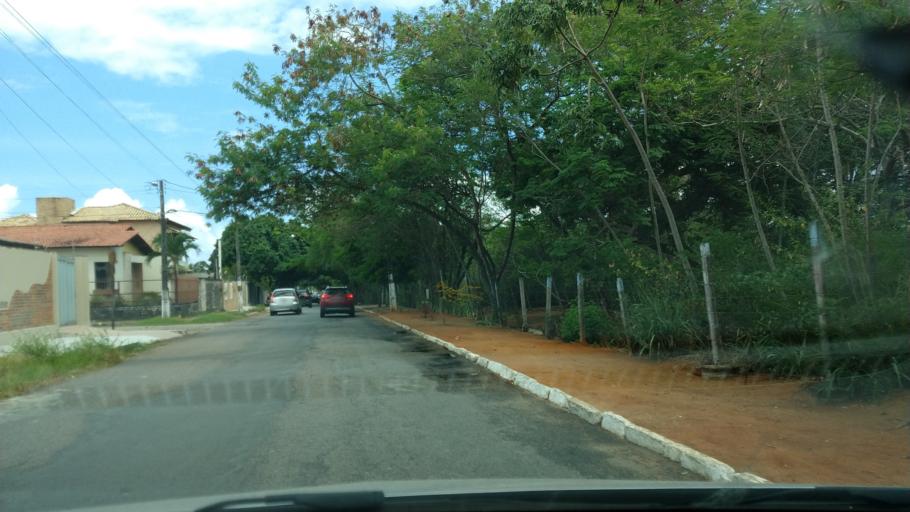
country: BR
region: Rio Grande do Norte
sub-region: Natal
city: Natal
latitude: -5.8512
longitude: -35.1988
